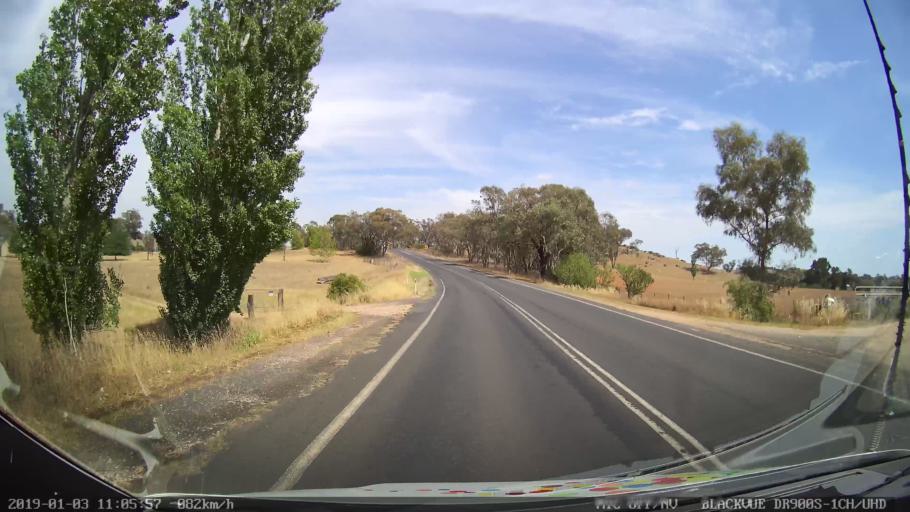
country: AU
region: New South Wales
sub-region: Young
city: Young
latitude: -34.2682
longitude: 148.2791
